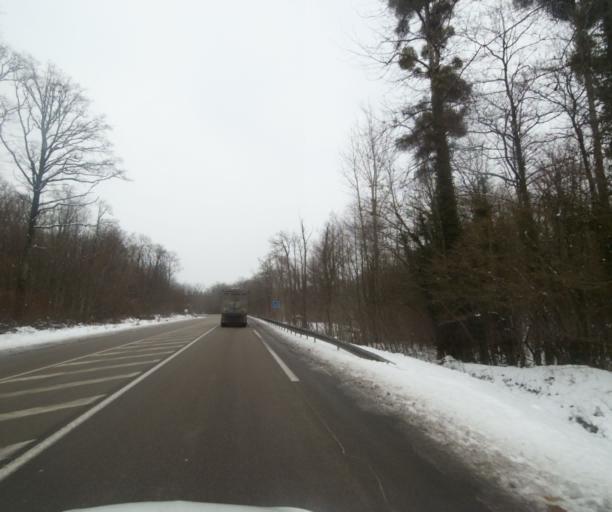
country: FR
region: Champagne-Ardenne
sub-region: Departement de la Haute-Marne
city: Saint-Dizier
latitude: 48.6075
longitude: 4.9126
